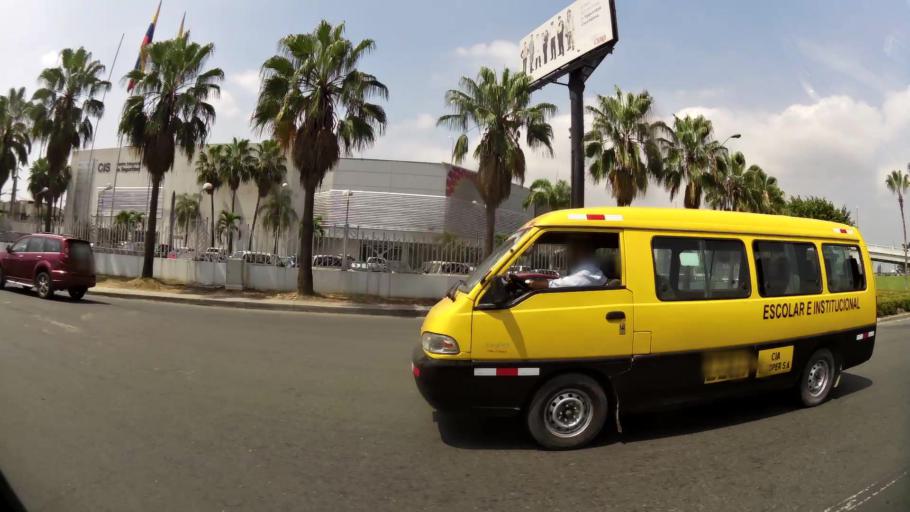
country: EC
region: Guayas
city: Eloy Alfaro
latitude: -2.1508
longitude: -79.8649
